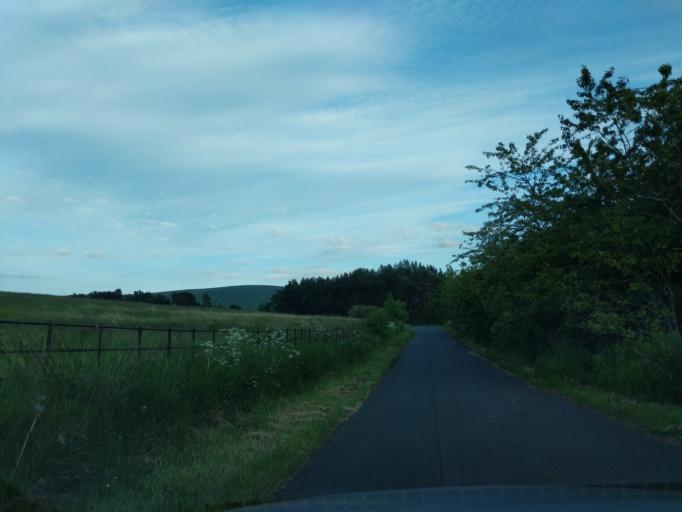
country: GB
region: Scotland
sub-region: Midlothian
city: Gorebridge
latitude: 55.7789
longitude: -3.1113
